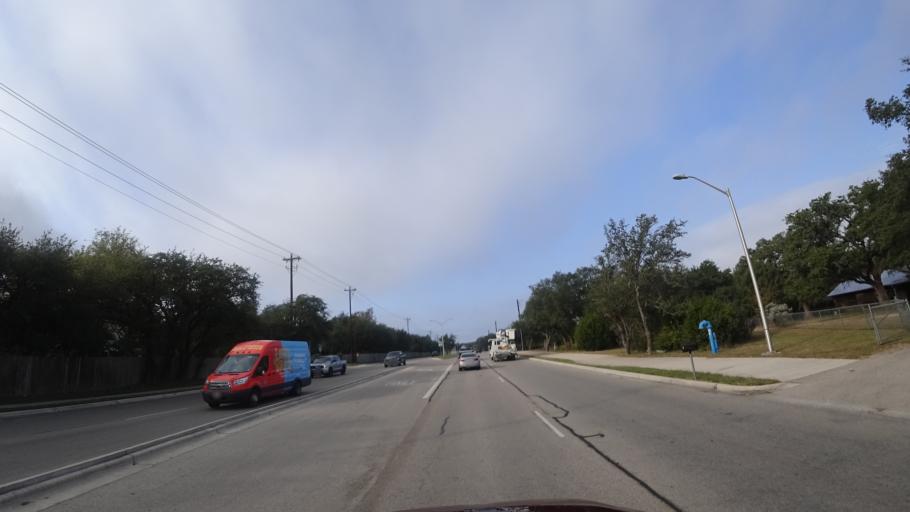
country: US
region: Texas
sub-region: Williamson County
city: Cedar Park
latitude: 30.5289
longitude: -97.8501
